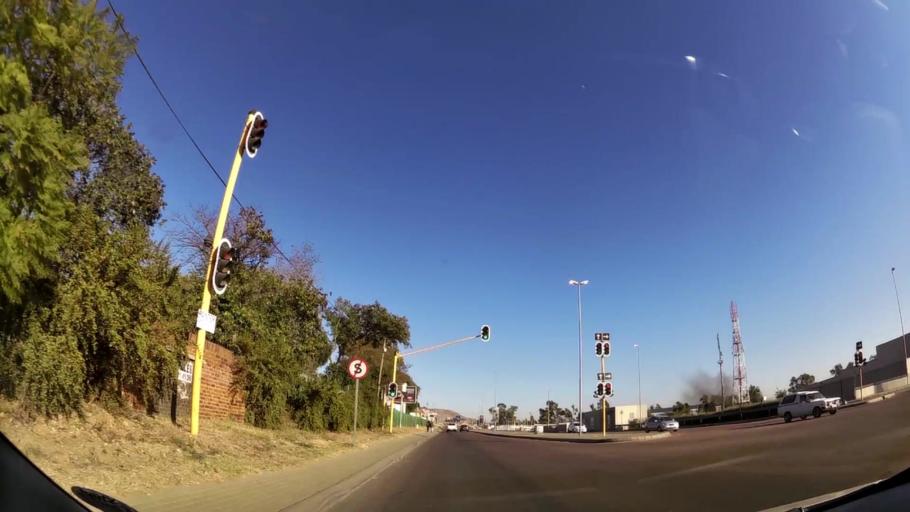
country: ZA
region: Gauteng
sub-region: West Rand District Municipality
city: Muldersdriseloop
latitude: -26.0622
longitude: 27.8355
